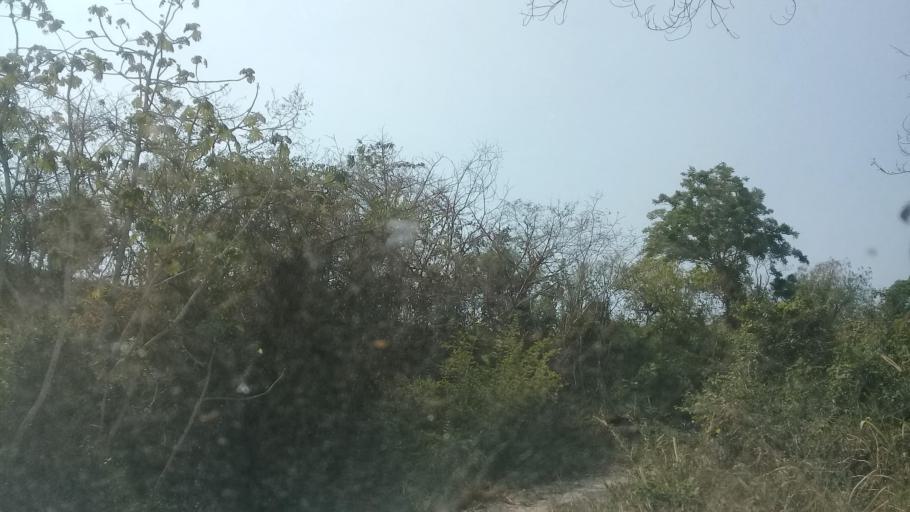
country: MX
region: Veracruz
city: El Castillo
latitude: 19.5746
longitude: -96.8020
